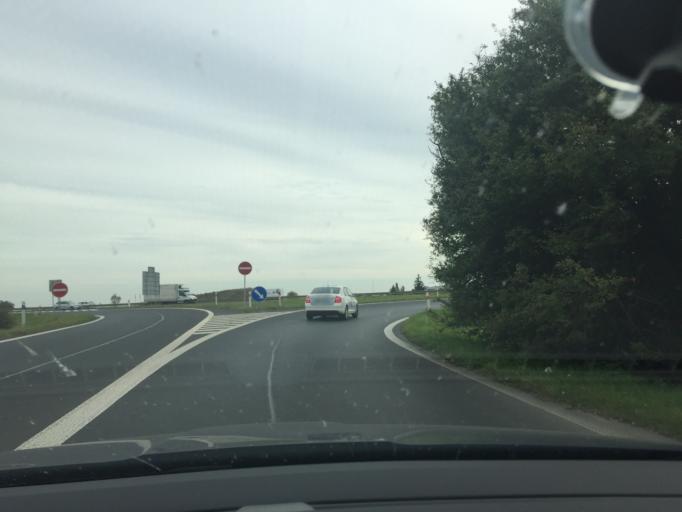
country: CZ
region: Praha
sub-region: Praha 20
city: Horni Pocernice
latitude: 50.1290
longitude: 14.6233
